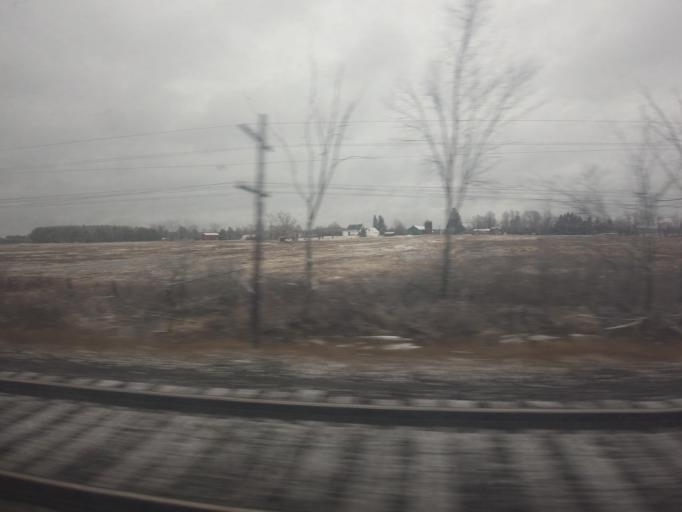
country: CA
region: Ontario
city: Gananoque
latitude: 44.3874
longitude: -76.0541
